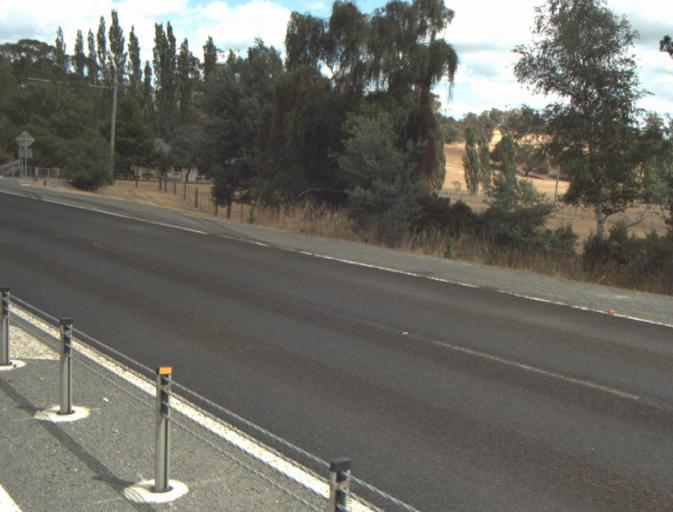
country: AU
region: Tasmania
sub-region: Launceston
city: Mayfield
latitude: -41.2937
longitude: 147.0481
